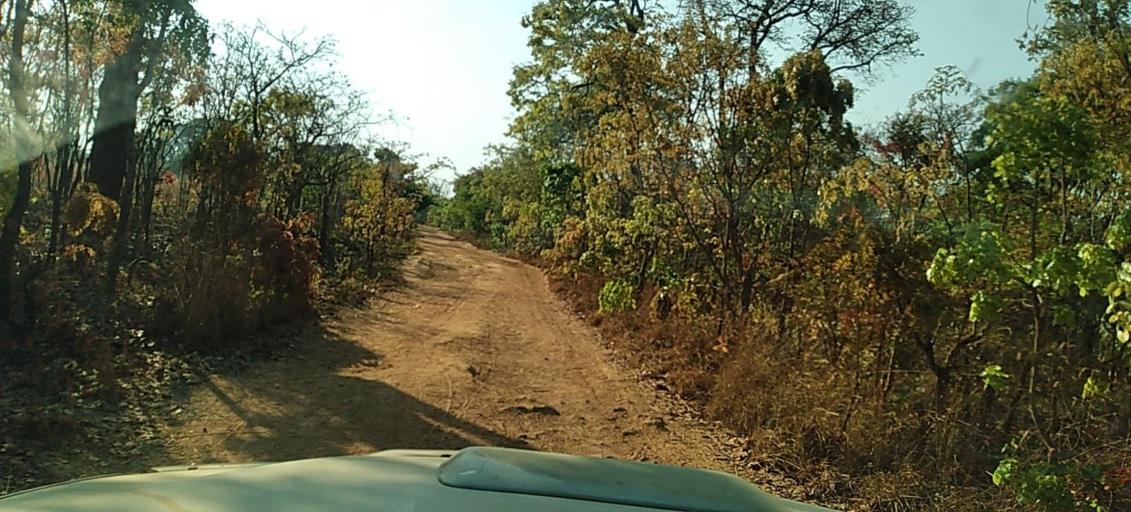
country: ZM
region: North-Western
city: Kasempa
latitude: -13.1848
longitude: 25.9559
